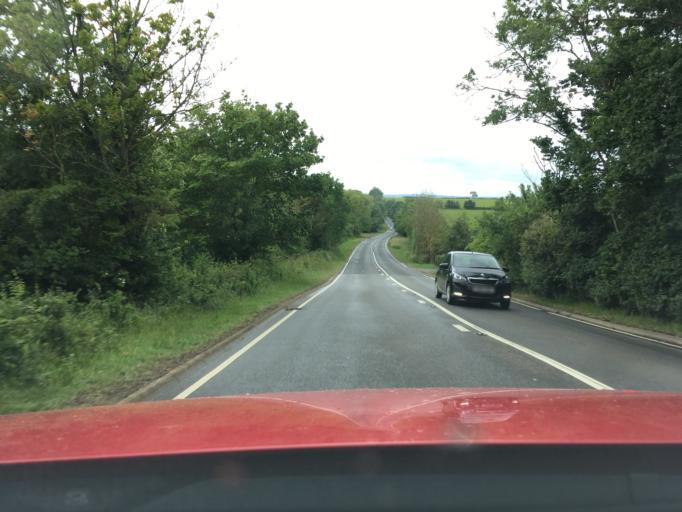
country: GB
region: England
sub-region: Warwickshire
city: Wellesbourne Mountford
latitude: 52.1296
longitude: -1.5996
